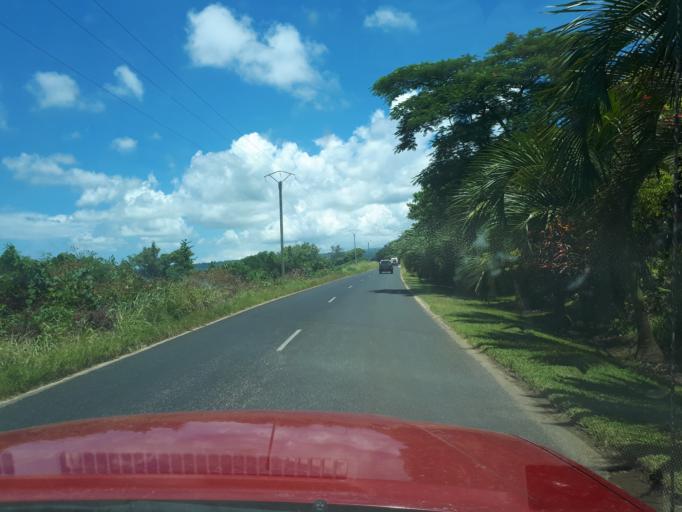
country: VU
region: Sanma
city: Luganville
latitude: -15.5154
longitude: 167.2037
